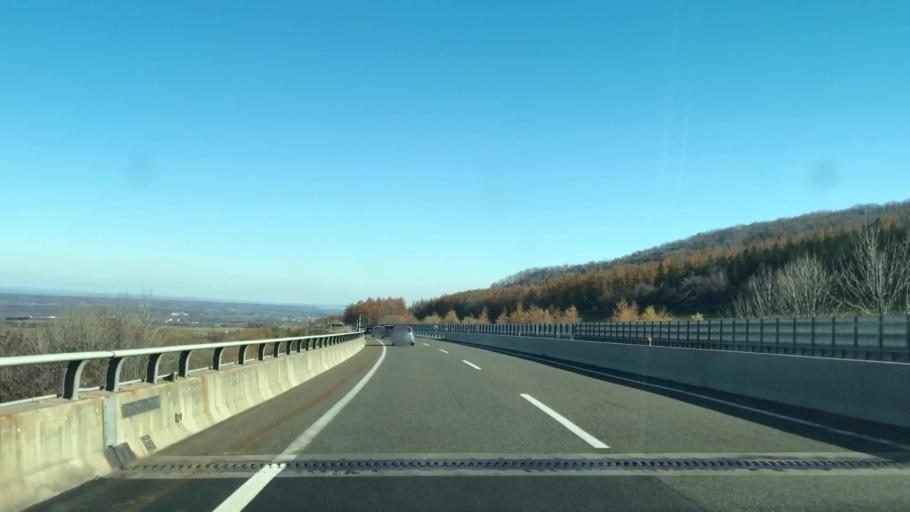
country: JP
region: Hokkaido
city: Otofuke
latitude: 43.0213
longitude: 142.8150
